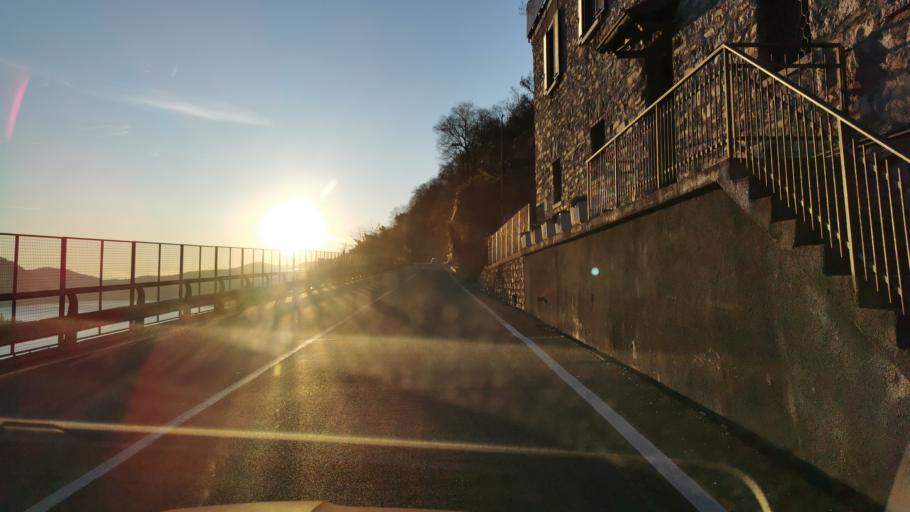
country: IT
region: Lombardy
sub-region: Provincia di Como
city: Carate Urio
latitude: 45.8748
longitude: 9.1267
